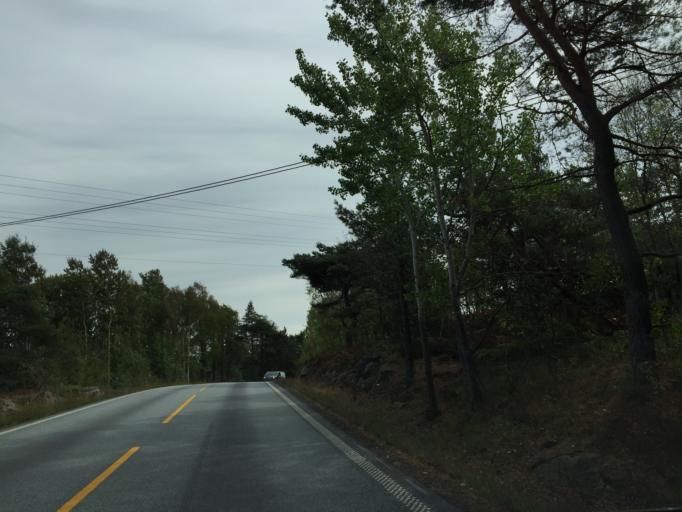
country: NO
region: Ostfold
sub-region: Hvaler
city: Skjaerhalden
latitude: 59.0658
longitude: 10.9370
